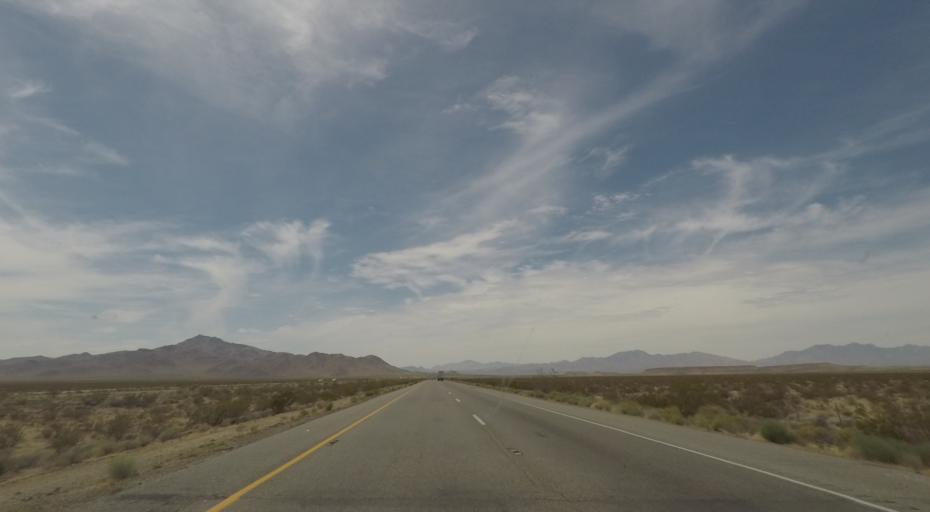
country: US
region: California
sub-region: San Bernardino County
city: Needles
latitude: 34.8046
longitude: -115.2783
